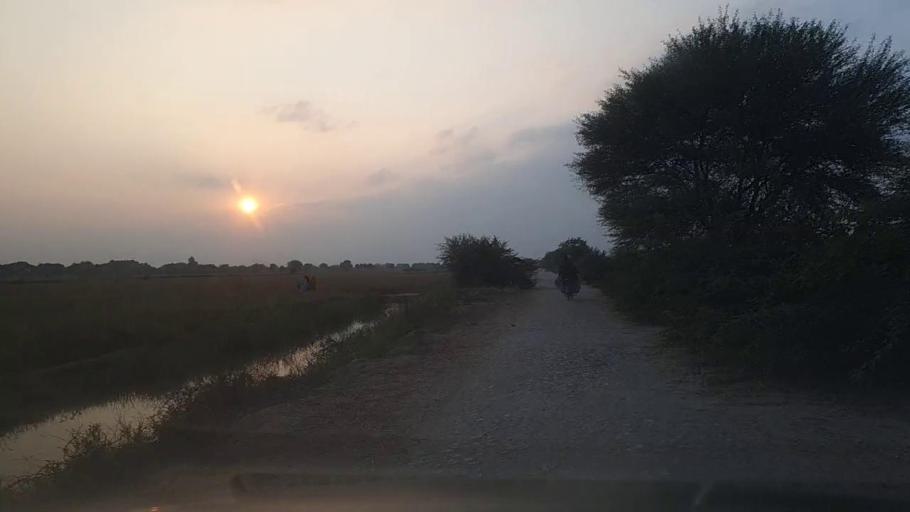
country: PK
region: Sindh
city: Jati
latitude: 24.5296
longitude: 68.3918
